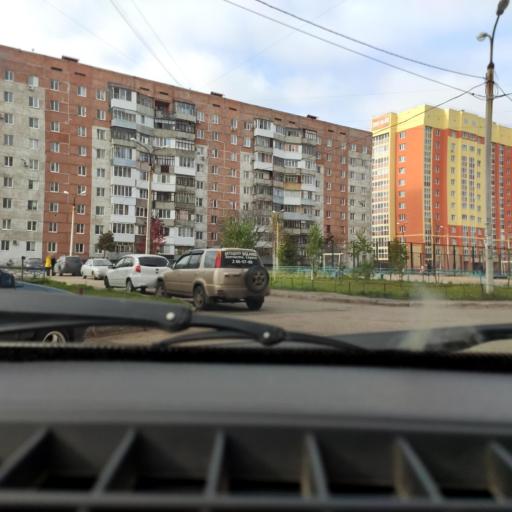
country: RU
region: Bashkortostan
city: Mikhaylovka
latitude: 54.7124
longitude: 55.8328
